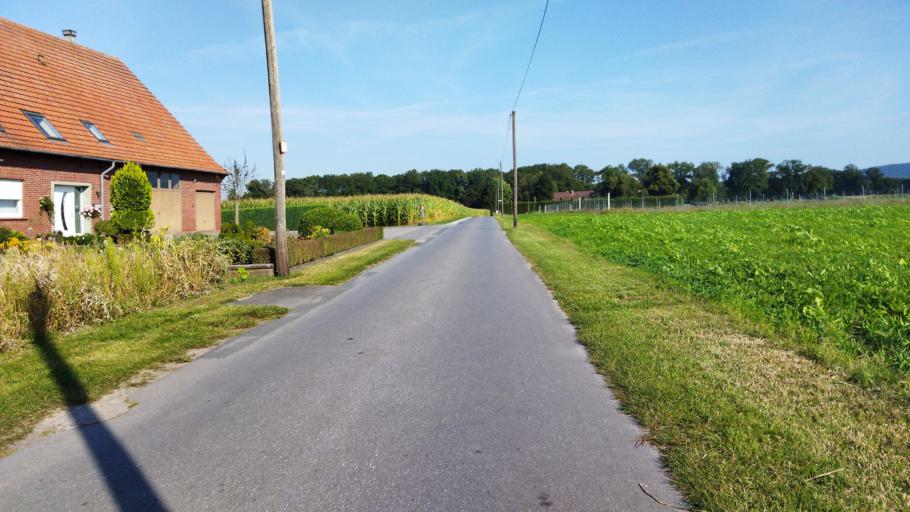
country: DE
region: Lower Saxony
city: Bad Laer
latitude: 52.1155
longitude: 8.0751
